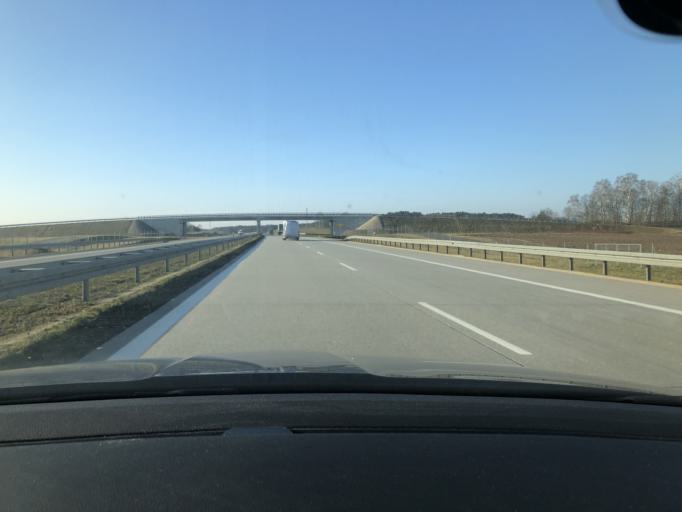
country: PL
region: Lubusz
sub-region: Powiat sulecinski
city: Torzym
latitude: 52.3234
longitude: 15.1779
